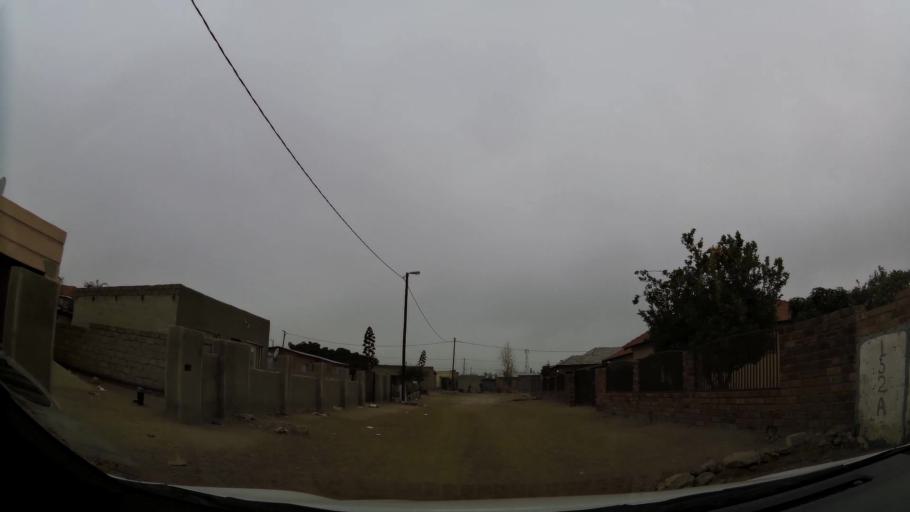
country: ZA
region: Limpopo
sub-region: Capricorn District Municipality
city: Polokwane
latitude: -23.8346
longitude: 29.3952
